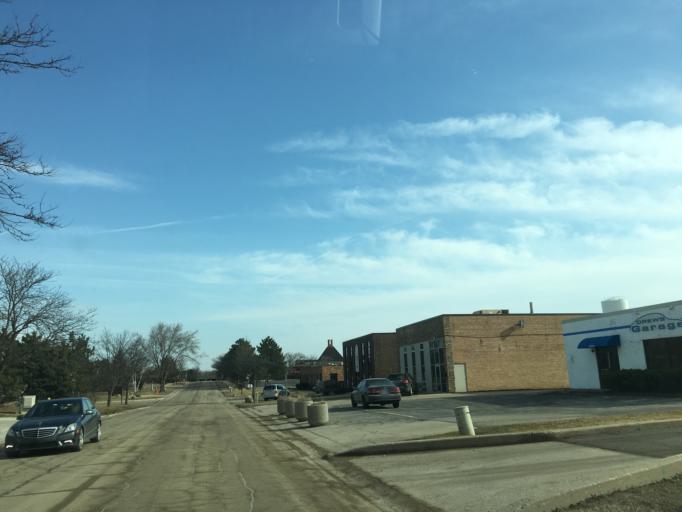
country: US
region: Illinois
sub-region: Cook County
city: Hoffman Estates
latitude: 42.0702
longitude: -88.0591
